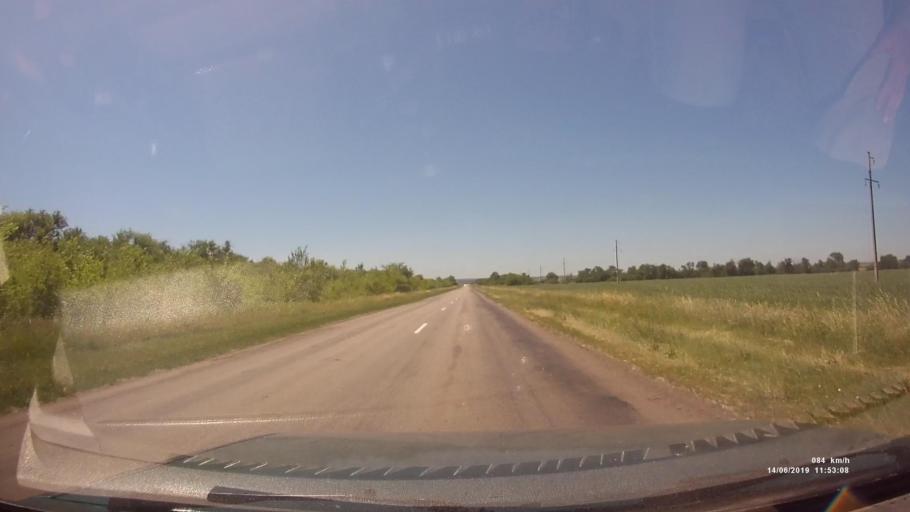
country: RU
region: Rostov
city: Kazanskaya
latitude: 49.8302
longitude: 41.2171
